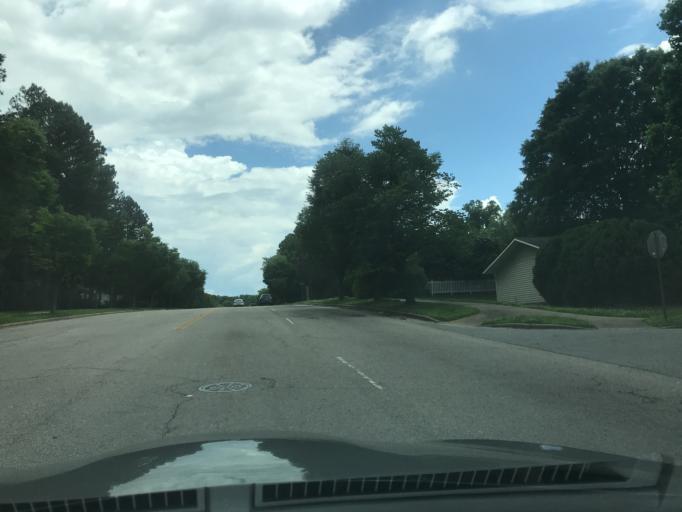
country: US
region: North Carolina
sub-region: Wake County
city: Raleigh
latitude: 35.8339
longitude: -78.5809
